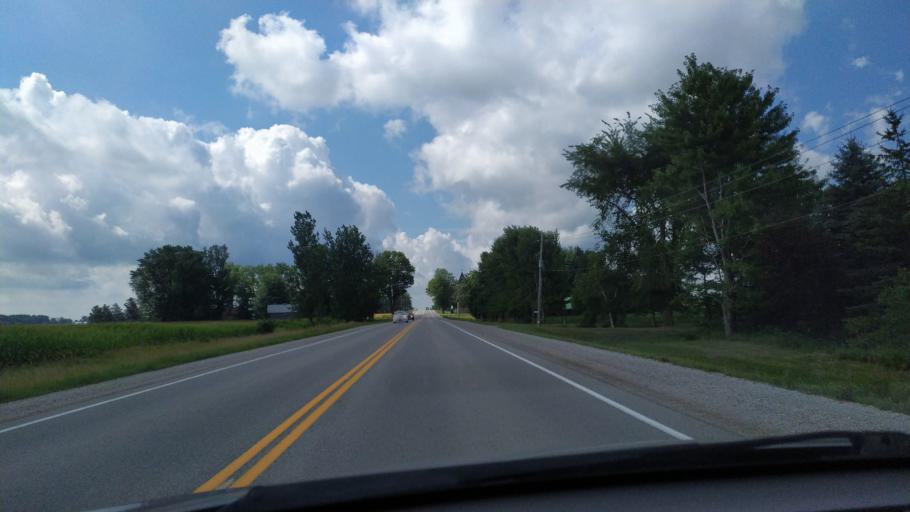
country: CA
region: Ontario
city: Huron East
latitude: 43.4231
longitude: -81.2363
